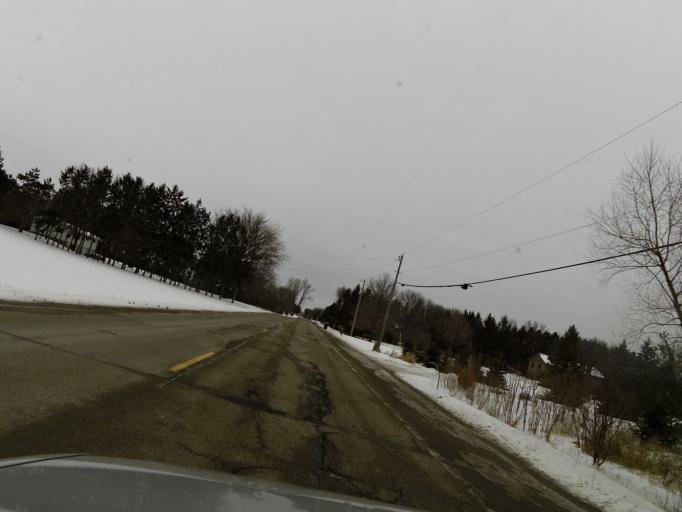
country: US
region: Minnesota
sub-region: Washington County
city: Oak Park Heights
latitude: 44.9872
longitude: -92.8225
